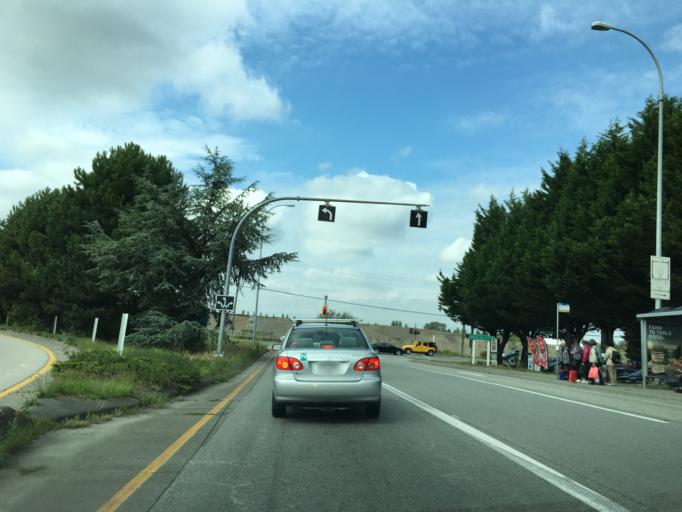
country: CA
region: British Columbia
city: Ladner
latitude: 49.1329
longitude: -123.0845
